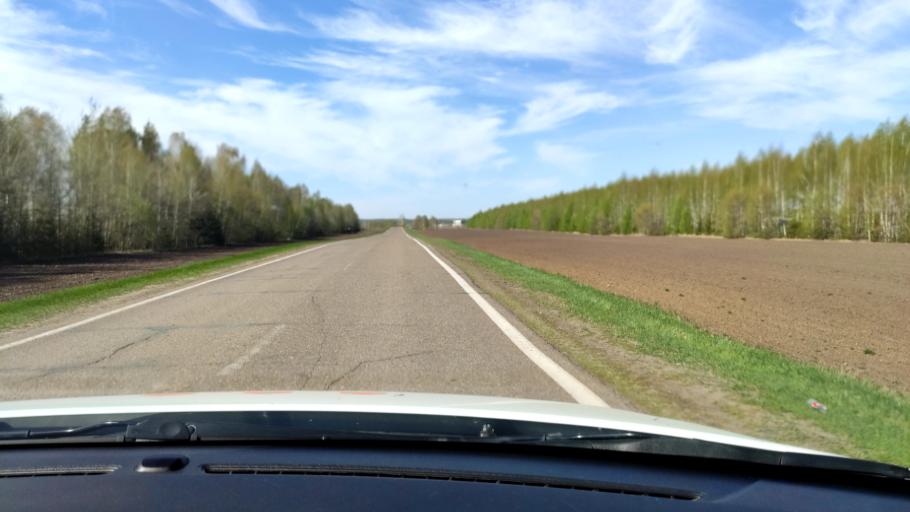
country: RU
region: Tatarstan
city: Stolbishchi
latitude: 55.5369
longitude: 49.2137
